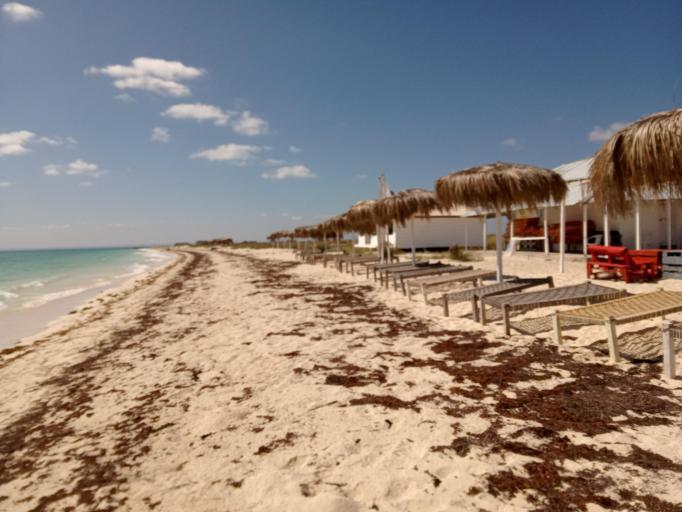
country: DJ
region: Djibouti
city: Djibouti
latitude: 11.7173
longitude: 43.2092
